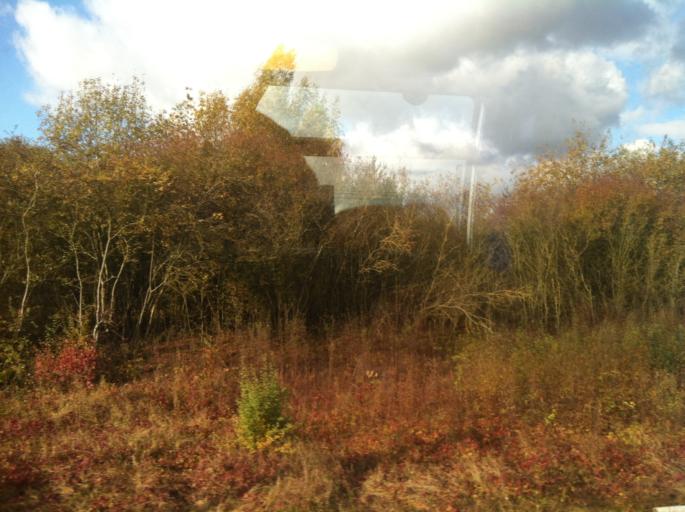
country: LU
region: Luxembourg
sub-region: Canton de Luxembourg
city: Hesperange
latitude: 49.5845
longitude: 6.1347
